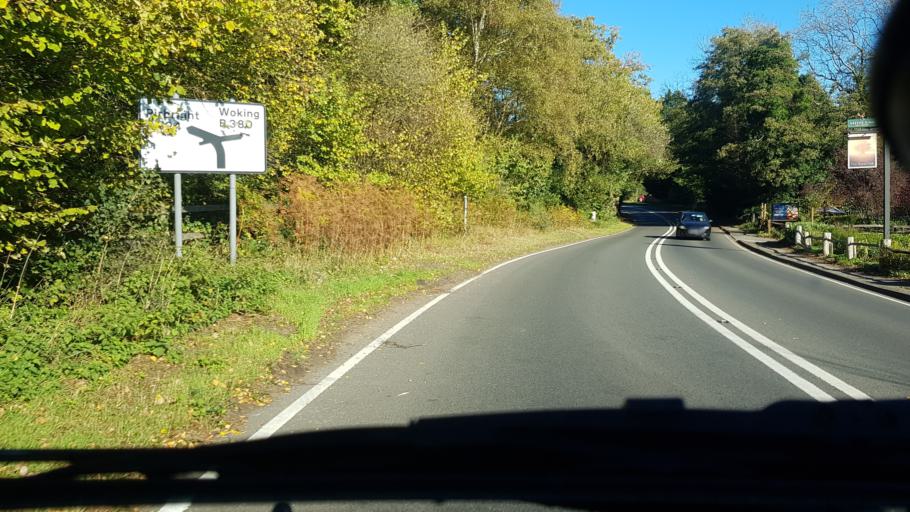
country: GB
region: England
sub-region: Surrey
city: Pirbright
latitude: 51.2803
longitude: -0.6477
